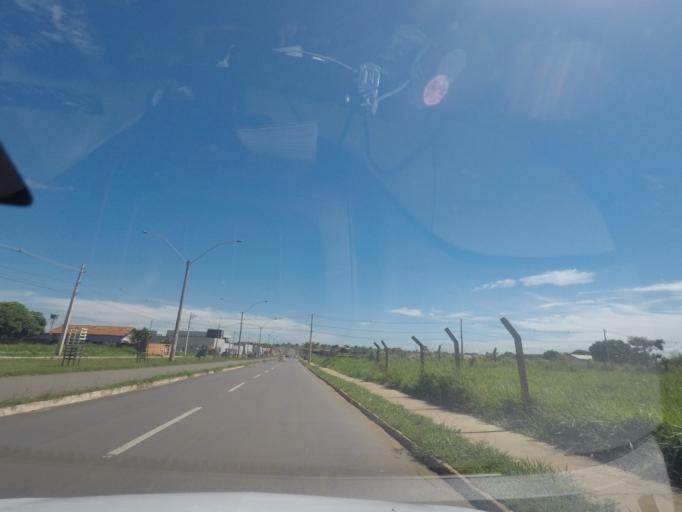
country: BR
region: Goias
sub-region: Aparecida De Goiania
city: Aparecida de Goiania
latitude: -16.8007
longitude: -49.3286
